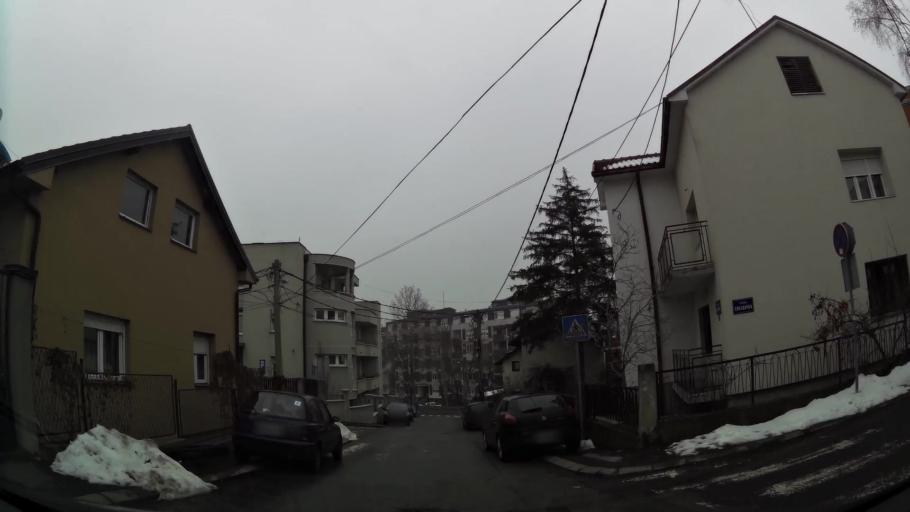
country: RS
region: Central Serbia
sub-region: Belgrade
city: Vozdovac
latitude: 44.7759
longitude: 20.4805
